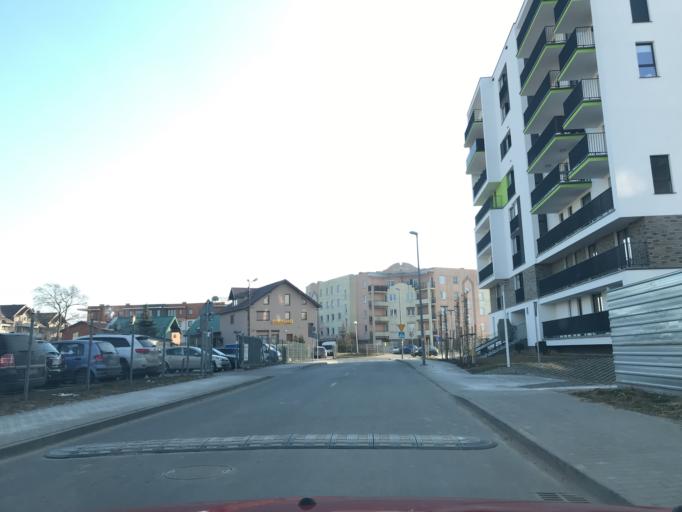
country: PL
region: Greater Poland Voivodeship
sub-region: Kalisz
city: Kalisz
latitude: 51.7616
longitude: 18.0643
